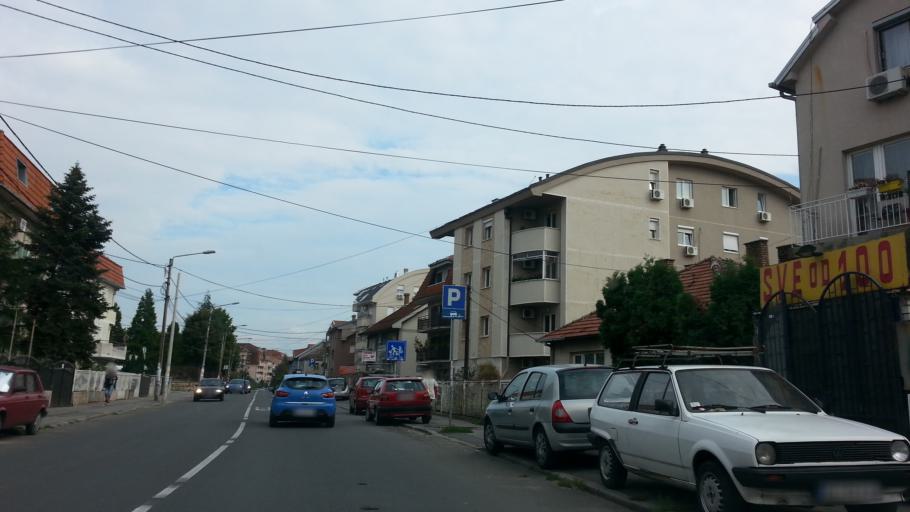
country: RS
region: Central Serbia
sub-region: Belgrade
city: Cukarica
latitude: 44.7582
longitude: 20.4172
